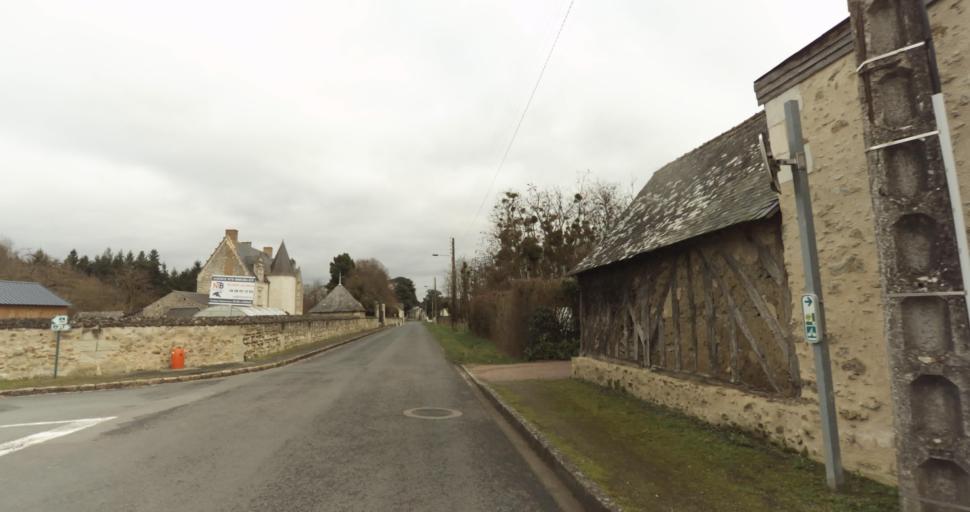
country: FR
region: Pays de la Loire
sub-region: Departement de Maine-et-Loire
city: Saint-Martin-de-la-Place
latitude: 47.3751
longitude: -0.1254
